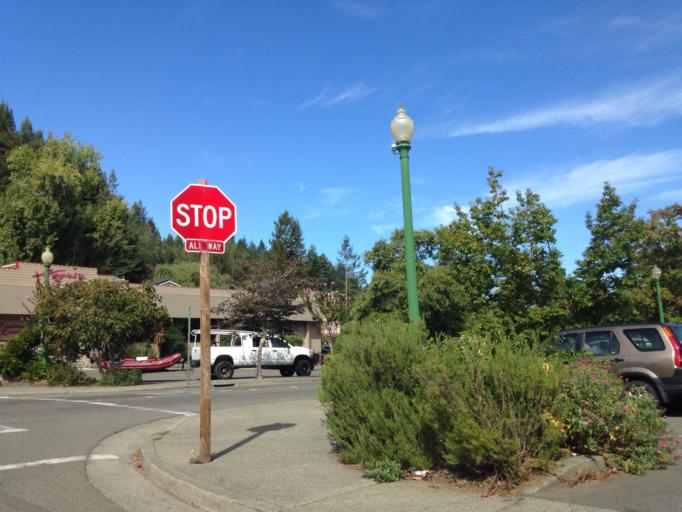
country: US
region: California
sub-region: Sonoma County
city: Occidental
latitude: 38.4074
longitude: -122.9475
